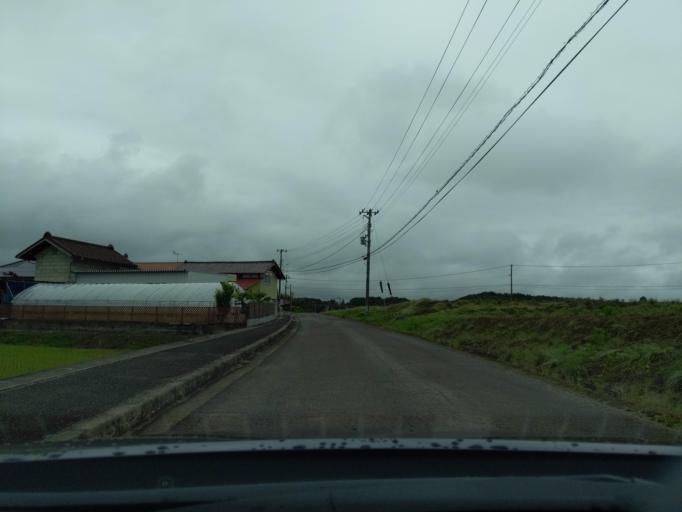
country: JP
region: Fukushima
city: Koriyama
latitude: 37.3668
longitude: 140.2878
